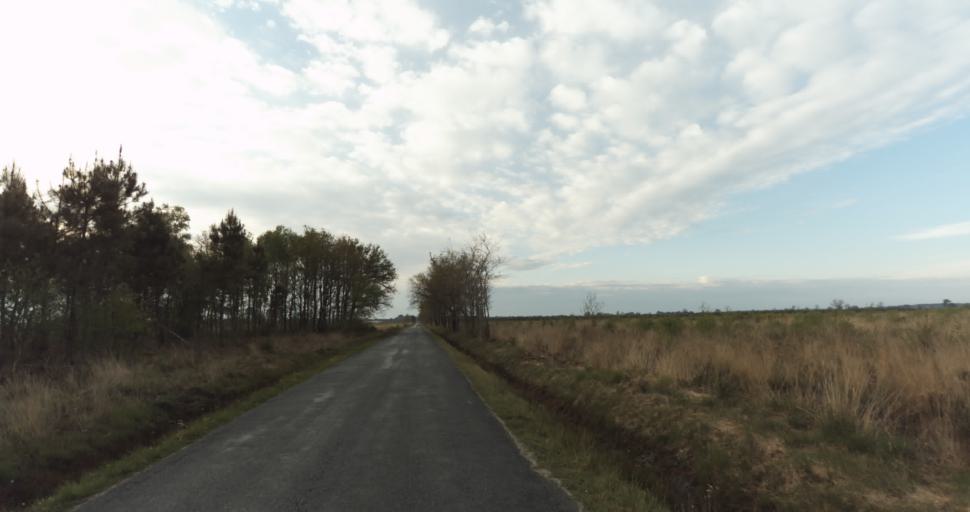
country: FR
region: Aquitaine
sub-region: Departement de la Gironde
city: Saint-Aubin-de-Medoc
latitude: 44.7850
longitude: -0.7511
